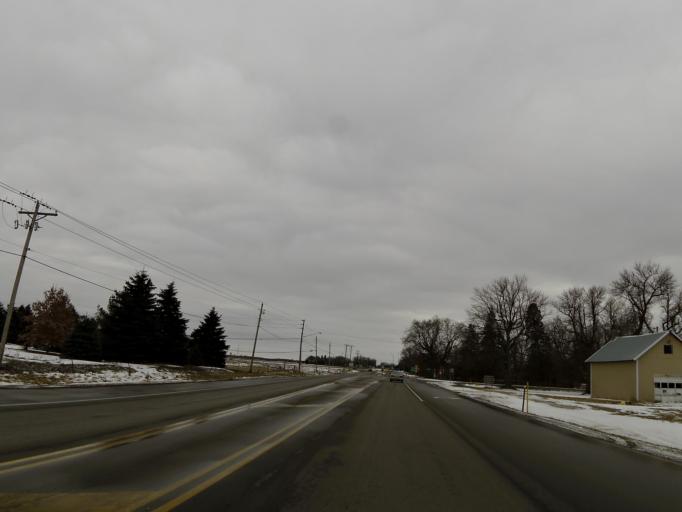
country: US
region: Minnesota
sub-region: Washington County
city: Cottage Grove
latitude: 44.8510
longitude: -92.9034
